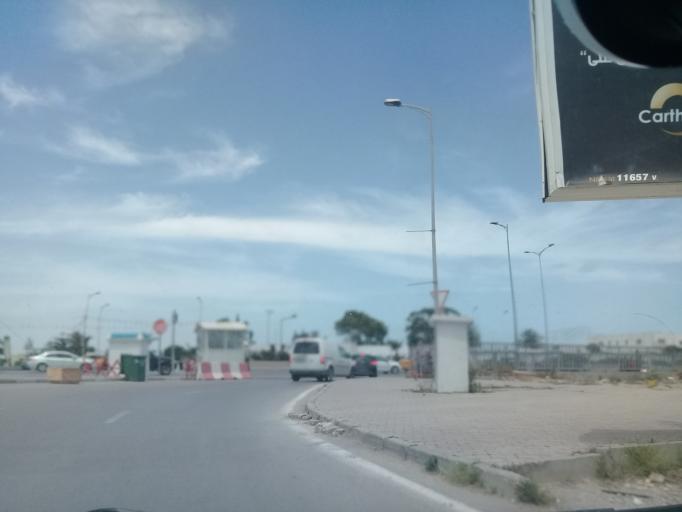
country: TN
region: Ariana
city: Ariana
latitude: 36.8389
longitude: 10.2372
